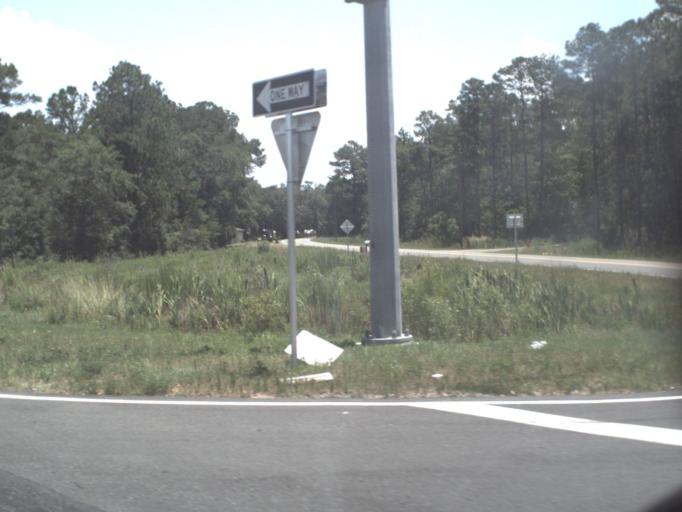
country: US
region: Florida
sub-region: Walton County
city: Freeport
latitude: 30.4670
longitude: -86.1304
